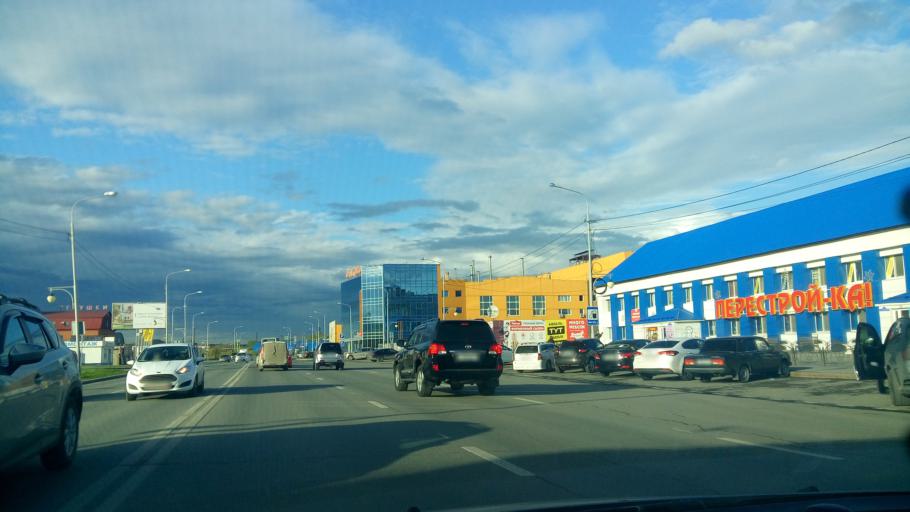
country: RU
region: Tjumen
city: Melioratorov
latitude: 57.1348
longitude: 65.6049
